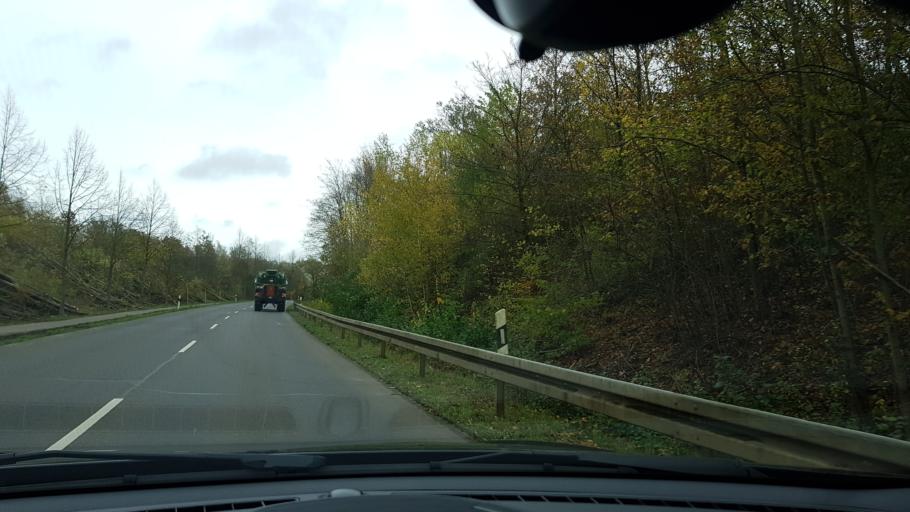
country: DE
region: North Rhine-Westphalia
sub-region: Regierungsbezirk Koln
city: Bedburg
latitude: 51.0399
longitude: 6.5687
